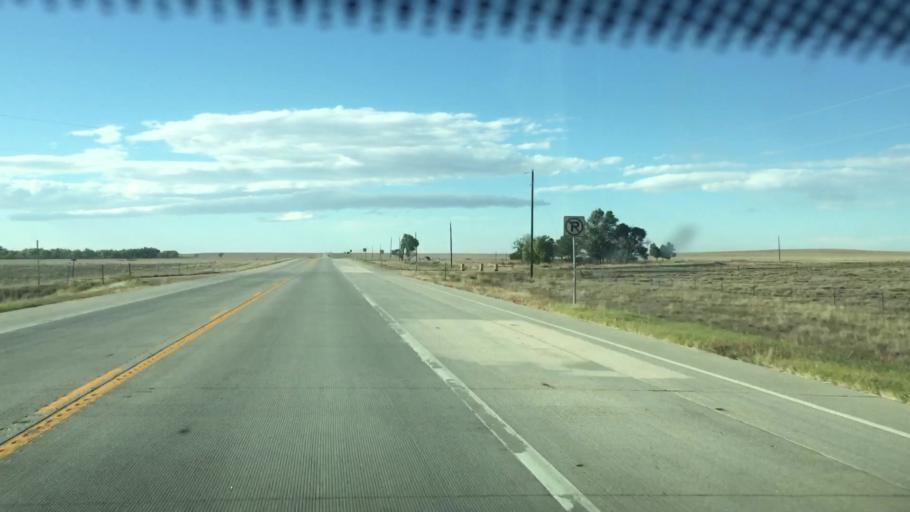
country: US
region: Colorado
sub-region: Lincoln County
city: Hugo
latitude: 39.0501
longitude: -103.3488
